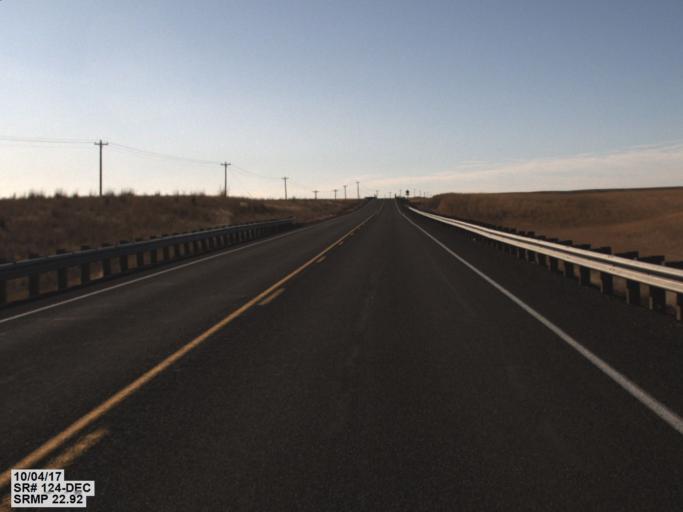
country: US
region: Washington
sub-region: Walla Walla County
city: Garrett
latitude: 46.2966
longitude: -118.5772
